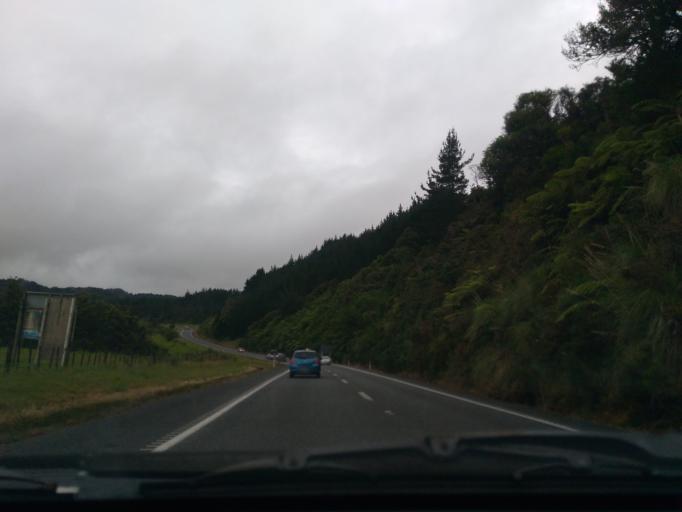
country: NZ
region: Northland
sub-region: Whangarei
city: Ruakaka
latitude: -36.0923
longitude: 174.4293
